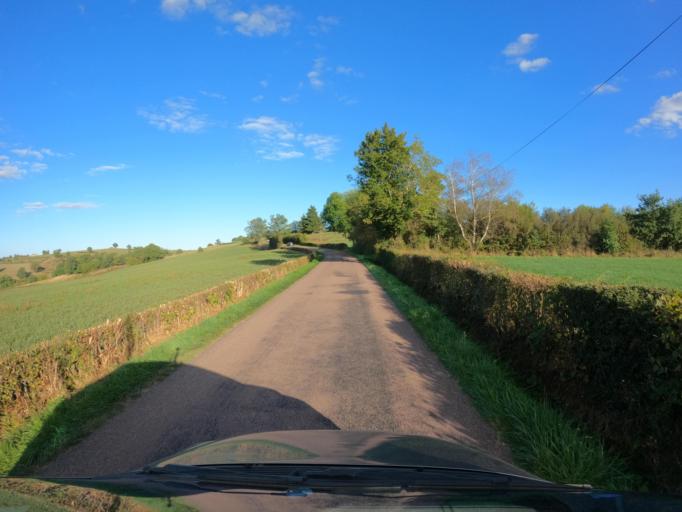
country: FR
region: Bourgogne
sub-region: Departement de Saone-et-Loire
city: Ecuisses
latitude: 46.7487
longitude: 4.5309
